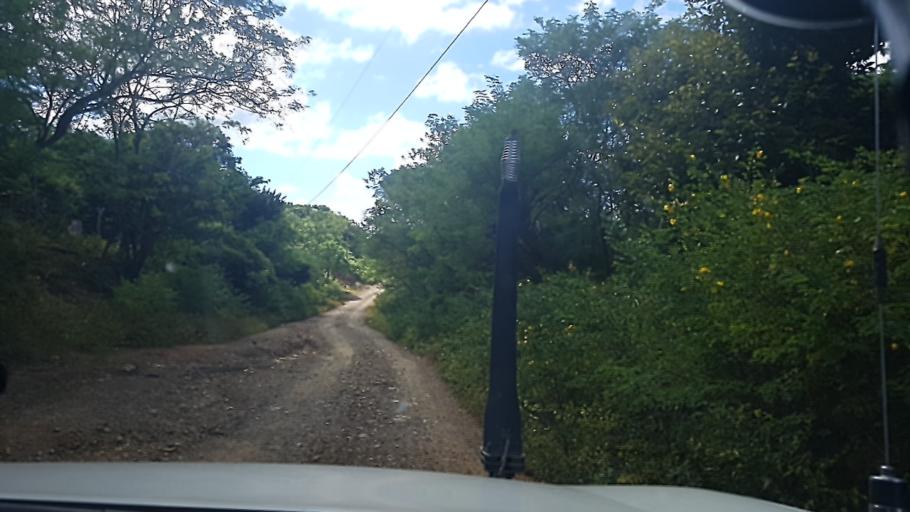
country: NI
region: Carazo
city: Santa Teresa
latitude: 11.6246
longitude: -86.1642
